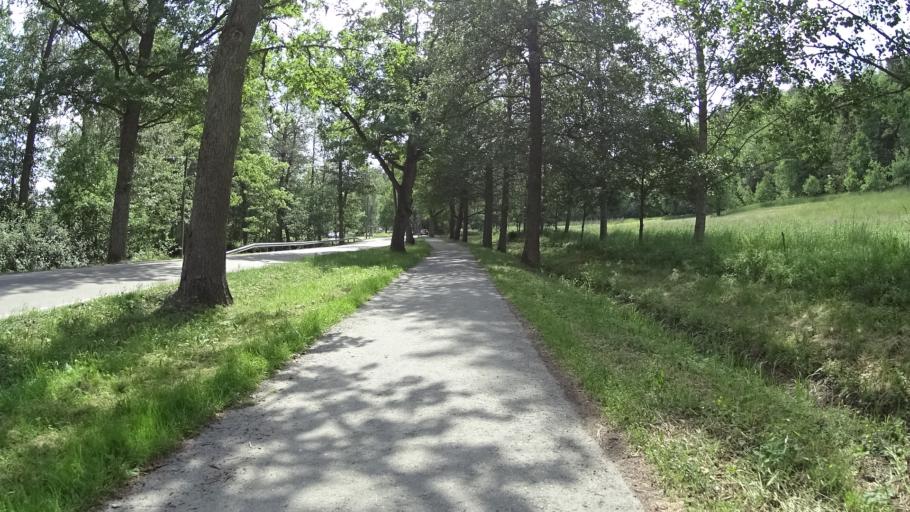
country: FI
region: Uusimaa
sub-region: Raaseporin
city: Pohja
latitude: 60.1262
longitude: 23.5373
